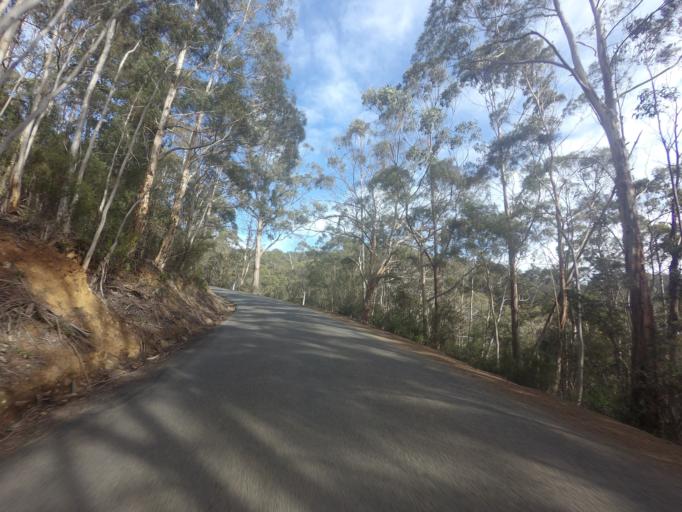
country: AU
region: Tasmania
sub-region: Kingborough
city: Margate
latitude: -43.0035
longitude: 147.1712
